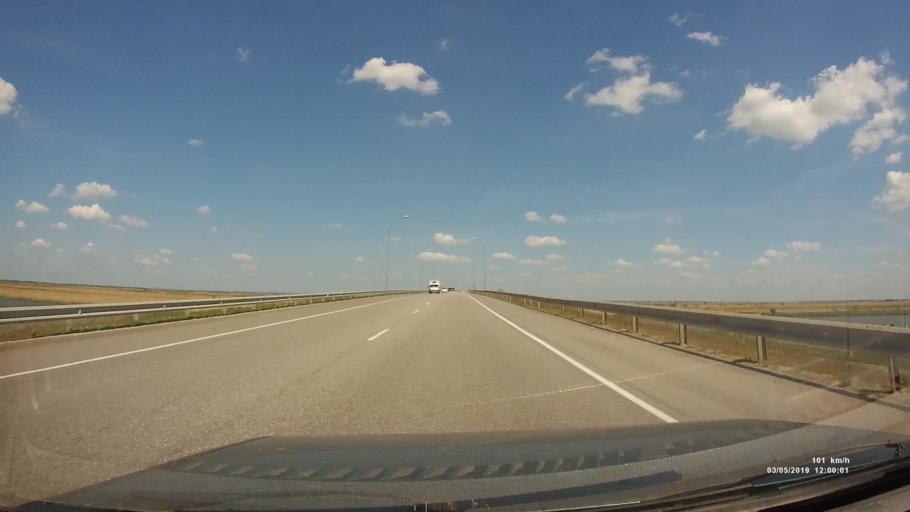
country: RU
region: Rostov
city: Bagayevskaya
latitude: 47.2431
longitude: 40.3360
